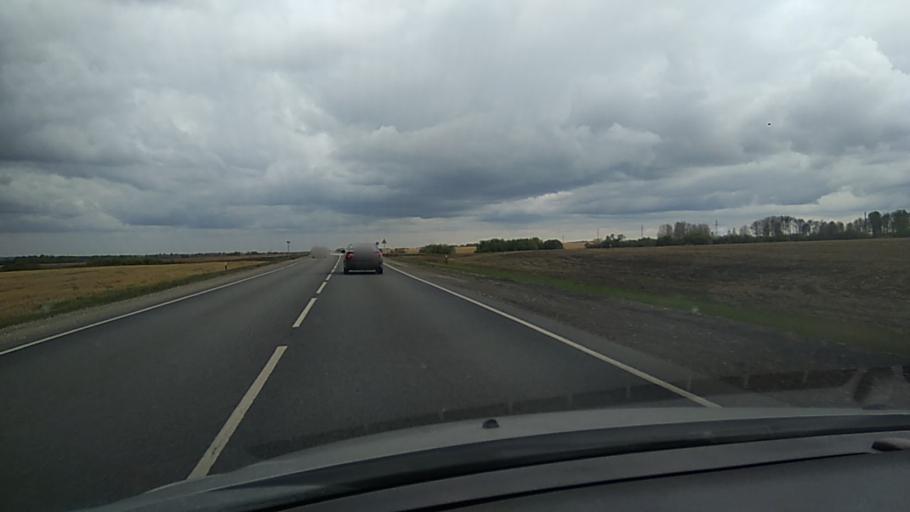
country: RU
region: Kurgan
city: Dalmatovo
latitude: 56.2895
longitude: 62.7870
